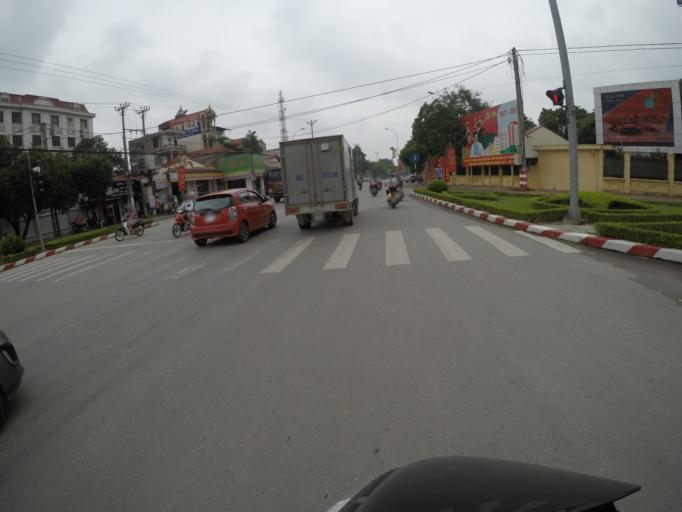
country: VN
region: Ha Noi
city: Soc Son
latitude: 21.2573
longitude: 105.8481
